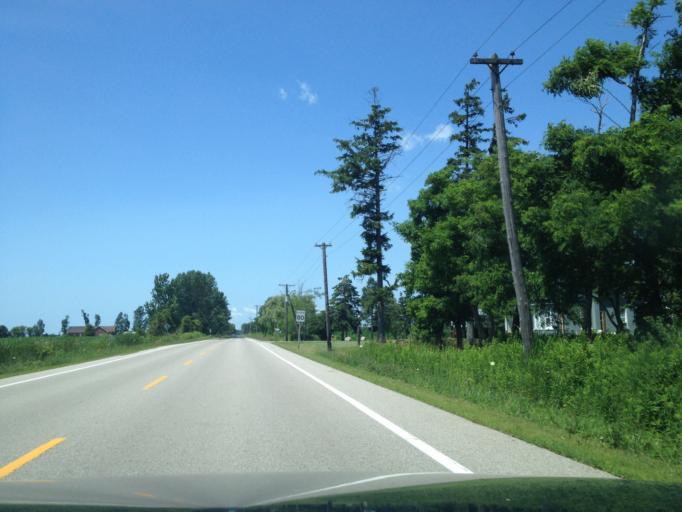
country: CA
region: Ontario
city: Norfolk County
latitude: 42.5789
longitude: -80.5657
